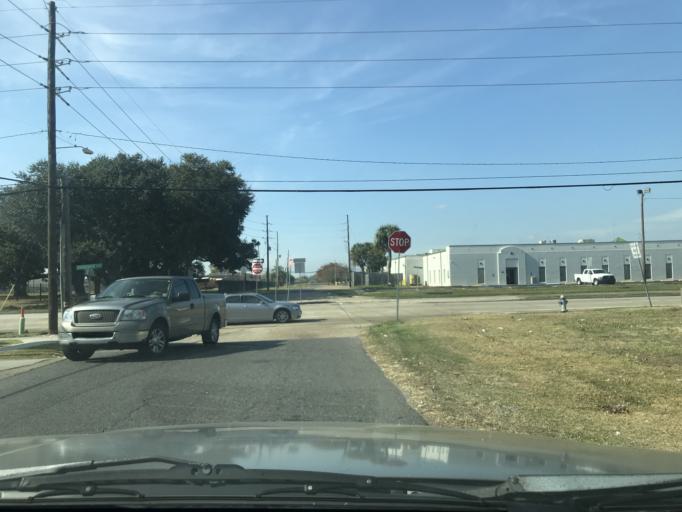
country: US
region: Louisiana
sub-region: Jefferson Parish
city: Marrero
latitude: 29.8932
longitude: -90.0995
